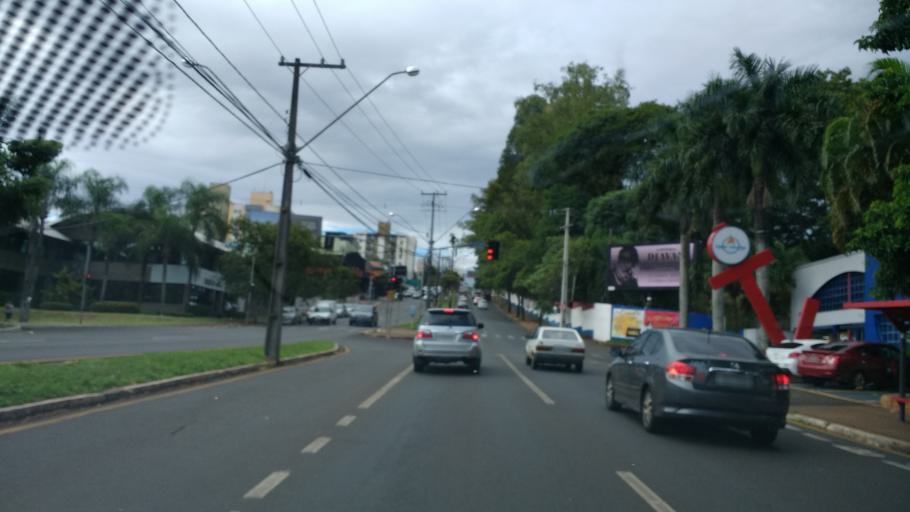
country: BR
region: Parana
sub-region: Londrina
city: Londrina
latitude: -23.3291
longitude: -51.1676
